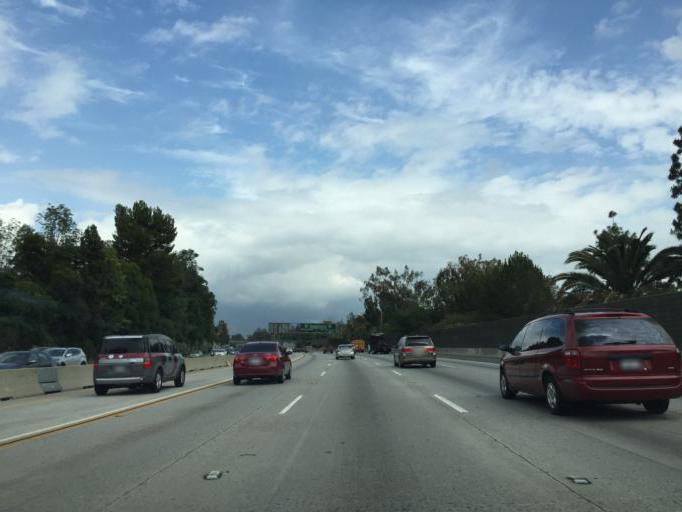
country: US
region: California
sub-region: Los Angeles County
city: Pasadena
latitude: 34.1412
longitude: -118.1767
